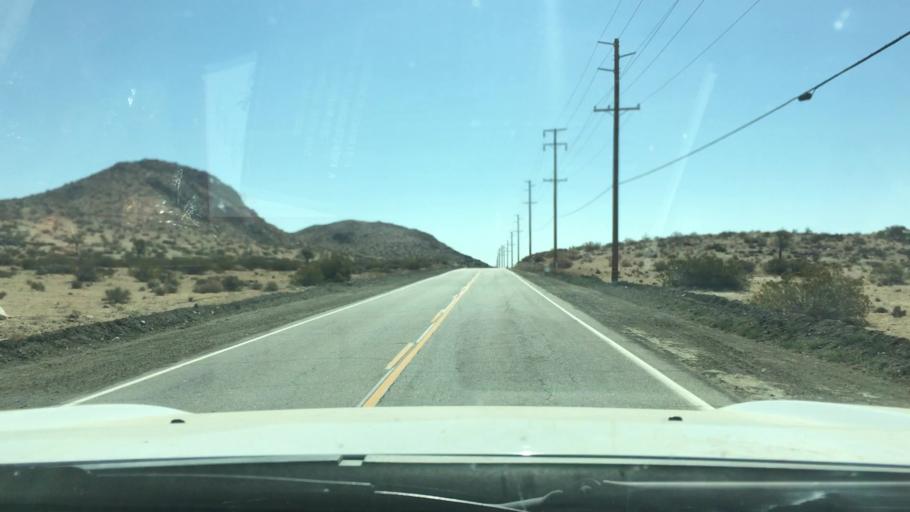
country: US
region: California
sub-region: Los Angeles County
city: Lake Los Angeles
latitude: 34.5798
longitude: -117.7396
